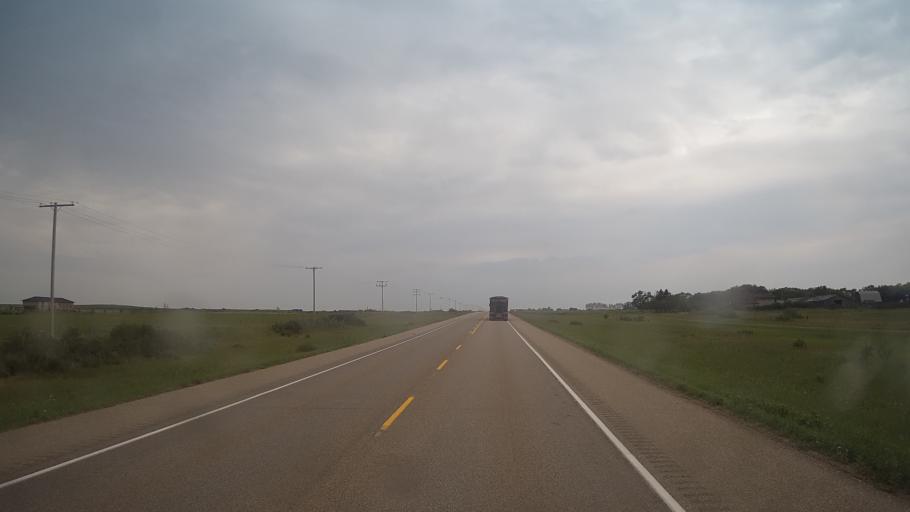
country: CA
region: Saskatchewan
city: Langham
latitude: 52.1289
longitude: -107.1644
